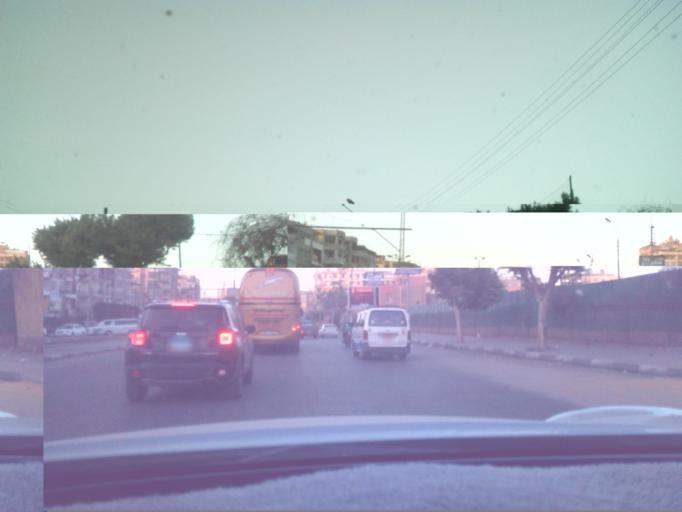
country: EG
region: Muhafazat al Qahirah
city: Cairo
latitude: 30.0970
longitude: 31.3427
